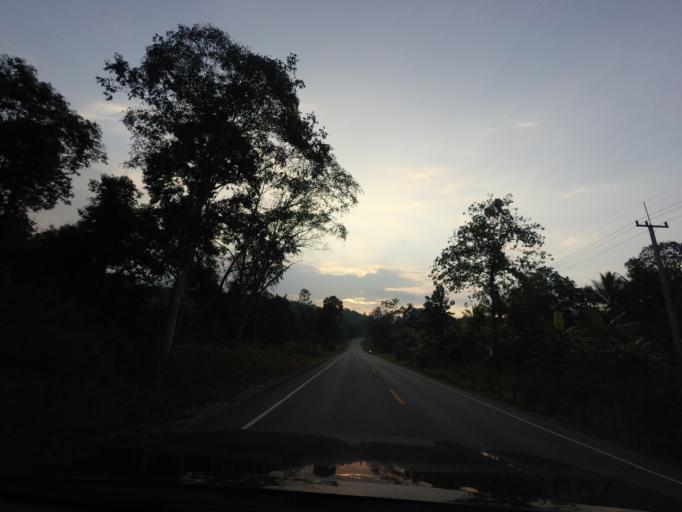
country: TH
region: Loei
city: Na Haeo
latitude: 17.4992
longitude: 101.0569
